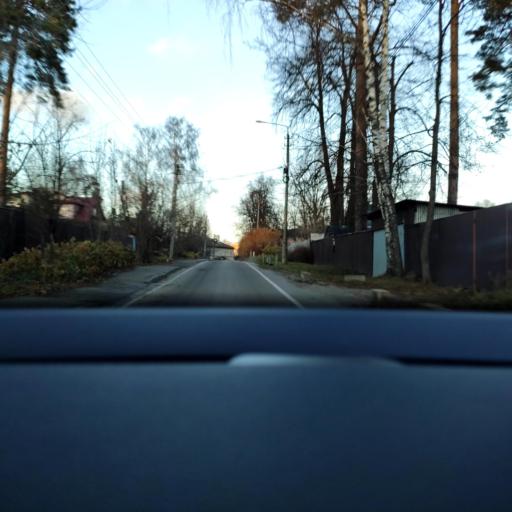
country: RU
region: Moskovskaya
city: Vidnoye
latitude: 55.5461
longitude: 37.6848
